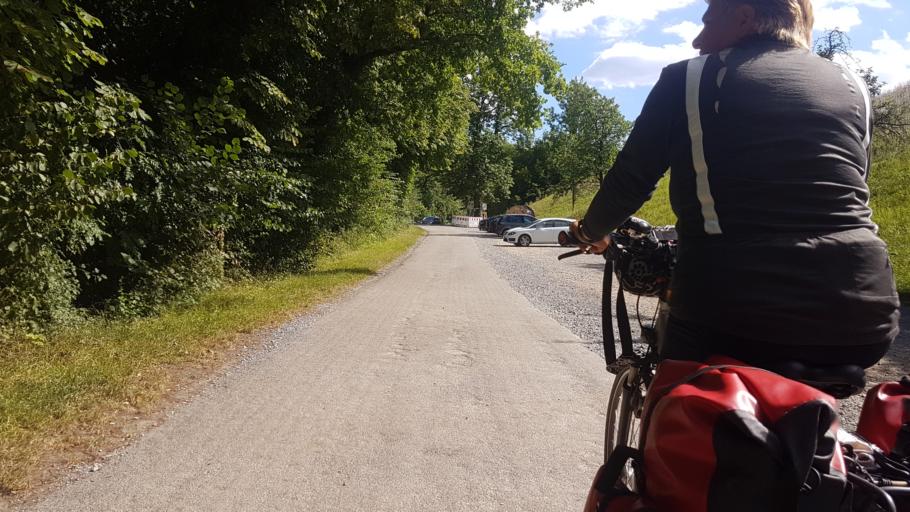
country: DE
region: Baden-Wuerttemberg
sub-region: Regierungsbezirk Stuttgart
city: Jagsthausen
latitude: 49.3313
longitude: 9.5029
